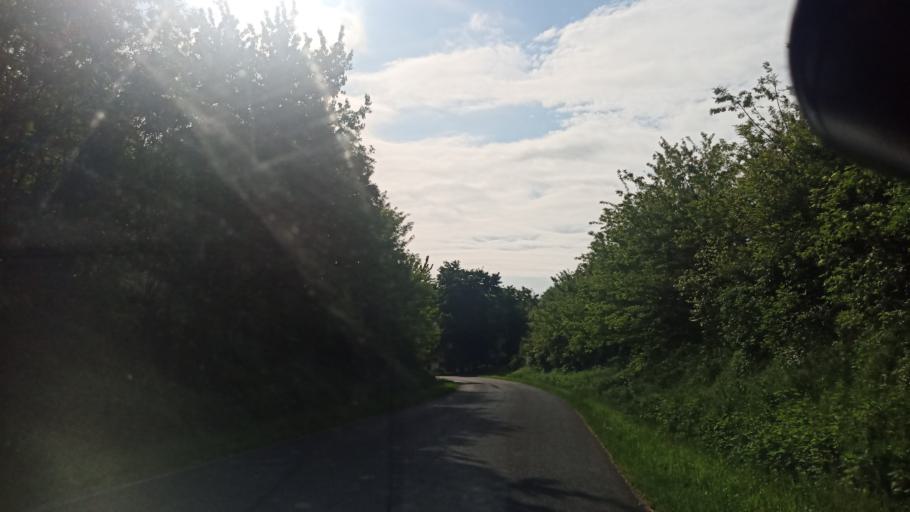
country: HU
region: Zala
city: Pacsa
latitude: 46.7033
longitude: 17.0554
